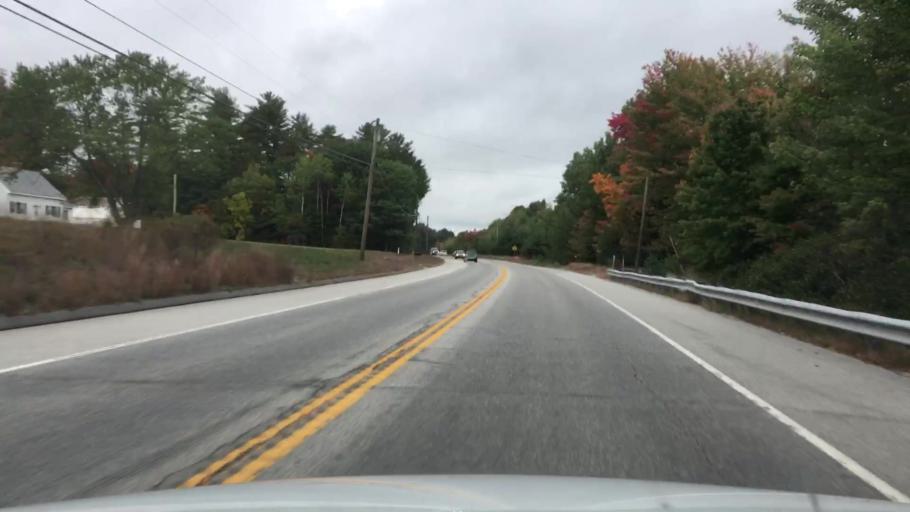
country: US
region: Maine
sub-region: Oxford County
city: Oxford
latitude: 44.1654
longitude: -70.5010
